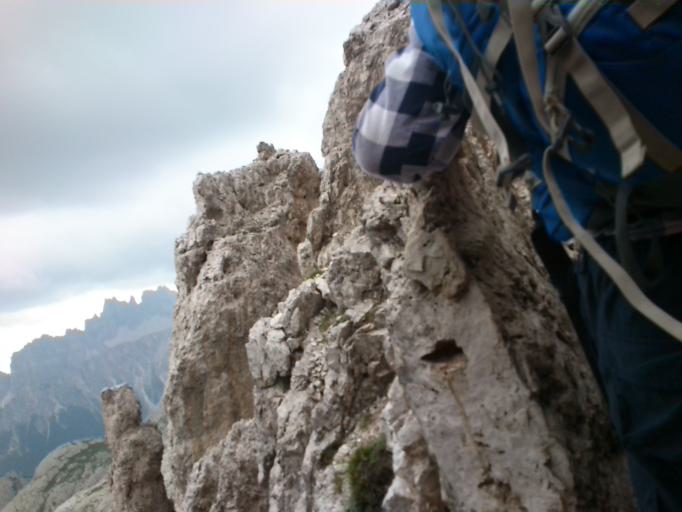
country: IT
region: Veneto
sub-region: Provincia di Belluno
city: Selva di Cadore
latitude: 46.5022
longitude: 12.0382
